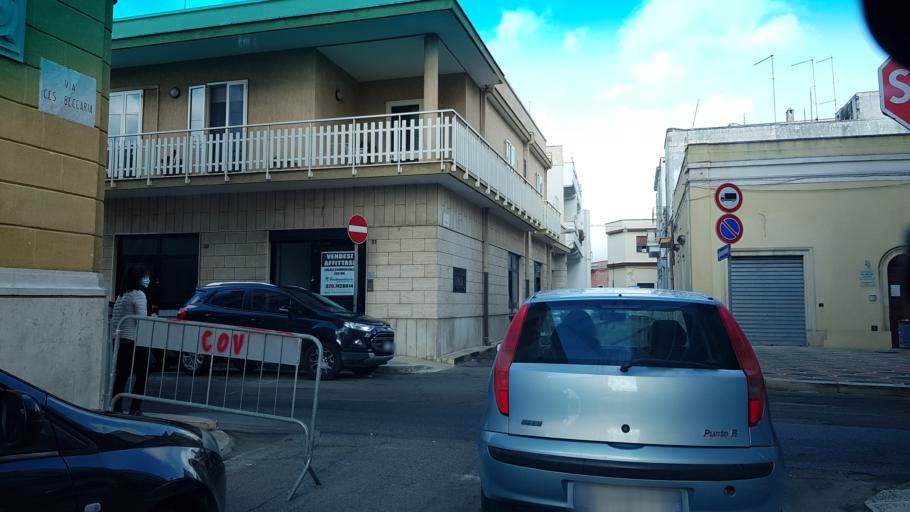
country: IT
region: Apulia
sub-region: Provincia di Brindisi
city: San Pietro Vernotico
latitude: 40.4882
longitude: 17.9981
